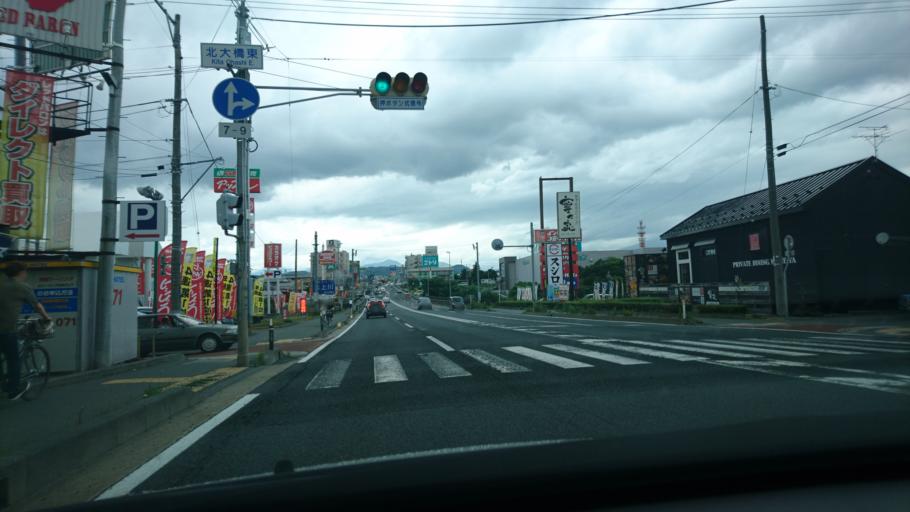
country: JP
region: Iwate
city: Morioka-shi
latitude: 39.7240
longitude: 141.1302
